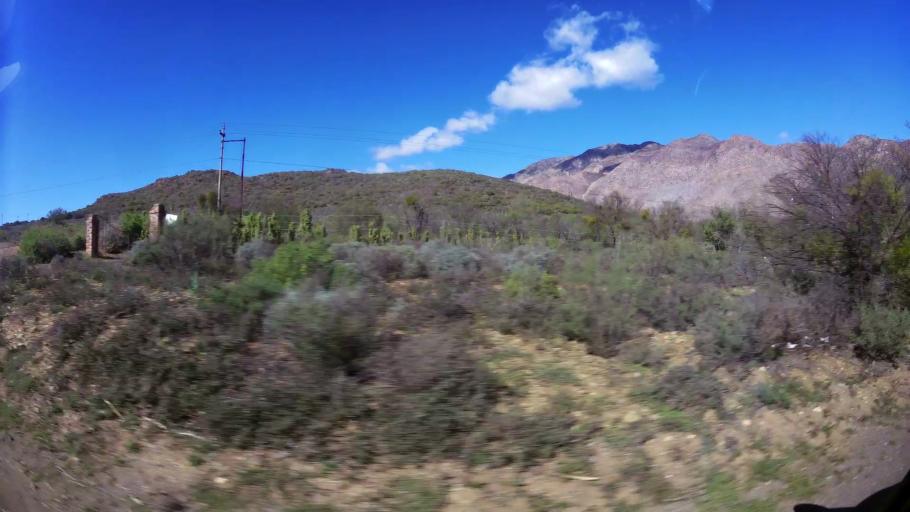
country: ZA
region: Western Cape
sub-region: Cape Winelands District Municipality
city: Ashton
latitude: -33.7910
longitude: 20.1295
